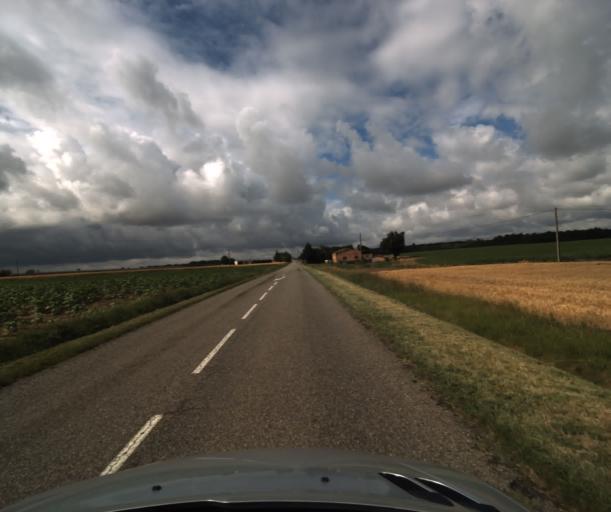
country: FR
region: Midi-Pyrenees
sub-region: Departement du Tarn-et-Garonne
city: Lavit
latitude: 43.9934
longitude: 0.9820
